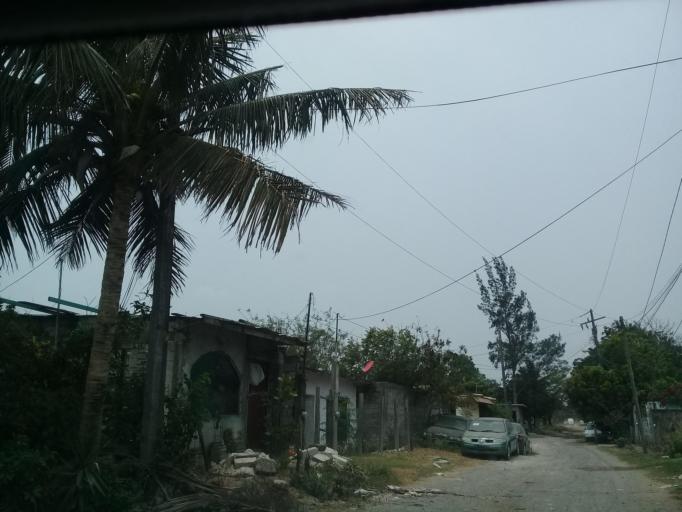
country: MX
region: Veracruz
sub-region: Veracruz
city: Las Amapolas
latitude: 19.1409
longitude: -96.2070
